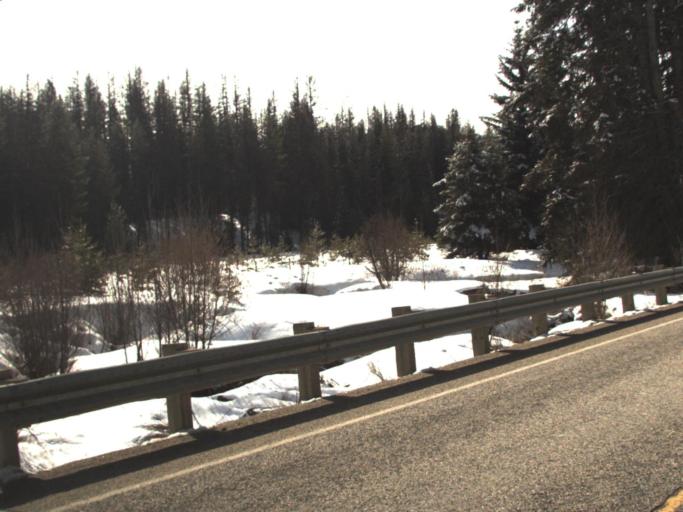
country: US
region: Washington
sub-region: Stevens County
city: Colville
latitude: 48.6640
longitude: -117.4762
